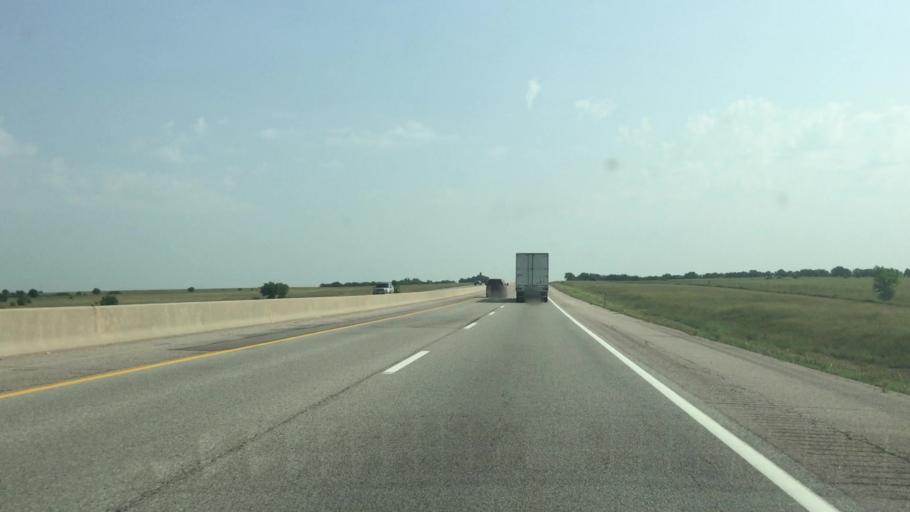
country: US
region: Kansas
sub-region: Butler County
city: El Dorado
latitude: 37.9721
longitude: -96.7199
